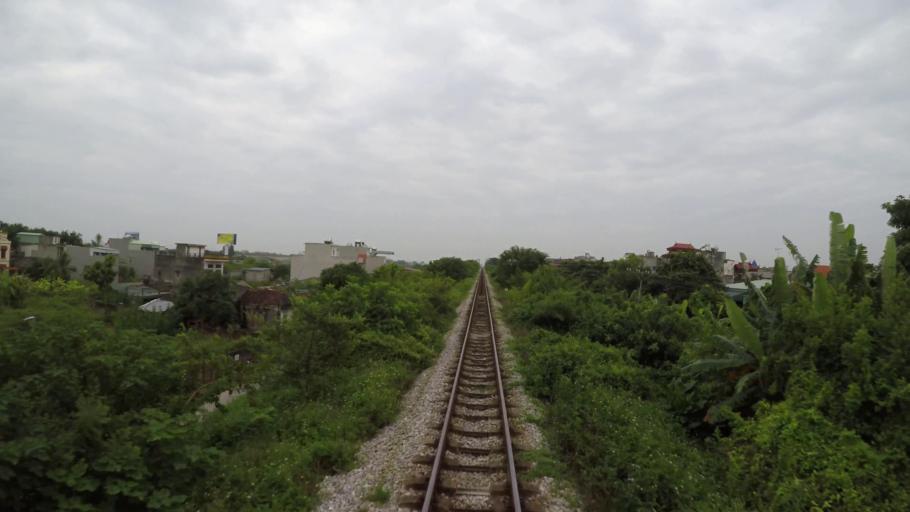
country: VN
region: Hai Duong
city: Thanh Pho Hai Duong
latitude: 20.9514
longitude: 106.3622
